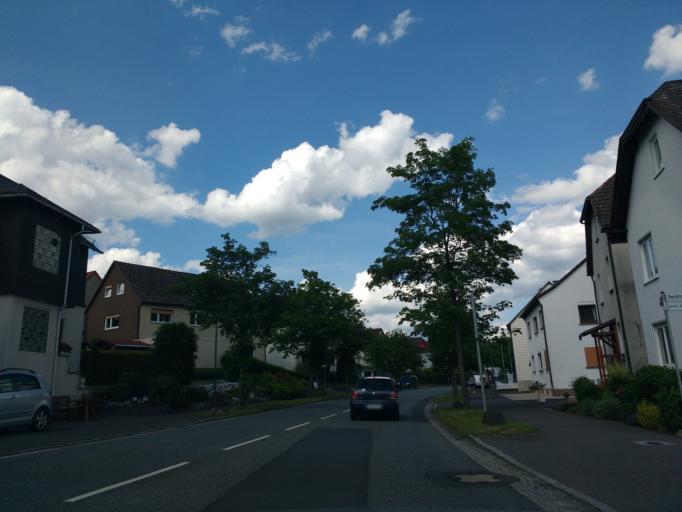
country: DE
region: Hesse
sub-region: Regierungsbezirk Giessen
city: Breidenbach
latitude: 50.9124
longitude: 8.4611
